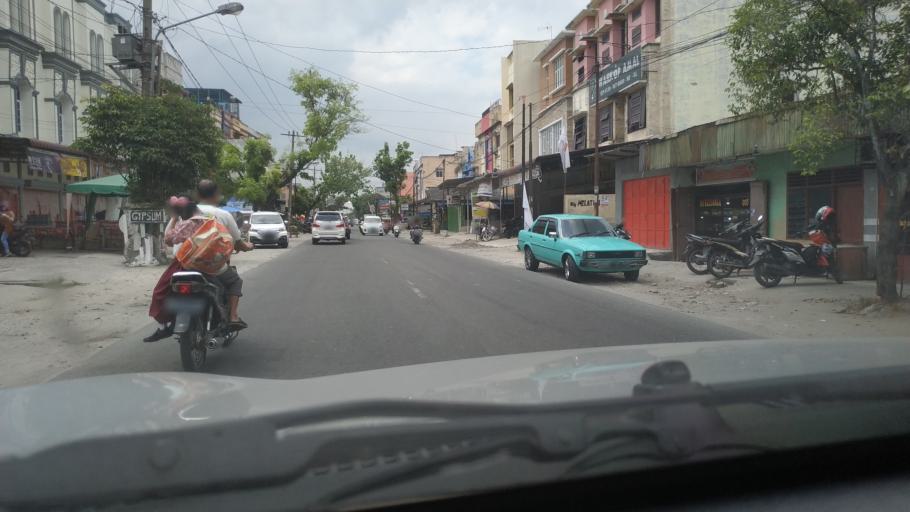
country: ID
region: North Sumatra
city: Sunggal
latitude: 3.5854
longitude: 98.6185
